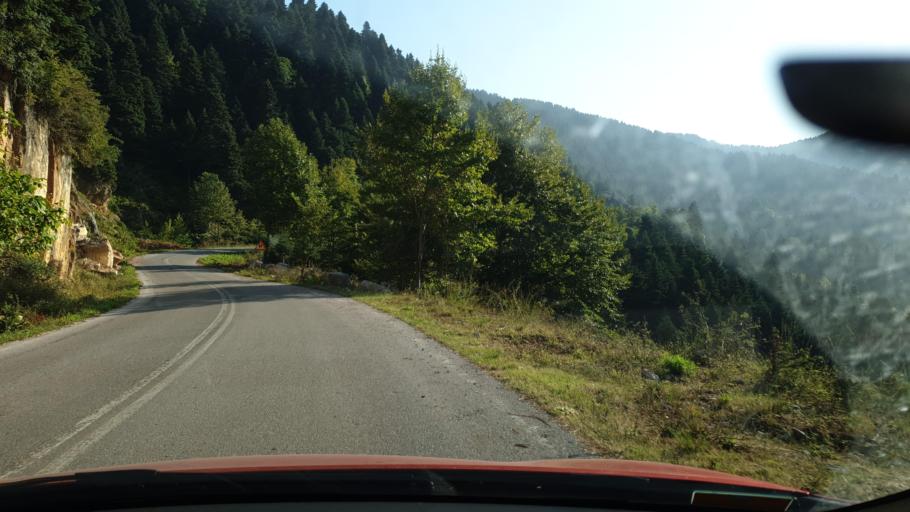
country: GR
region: Central Greece
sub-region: Nomos Evvoias
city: Yimnon
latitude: 38.5973
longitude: 23.8985
